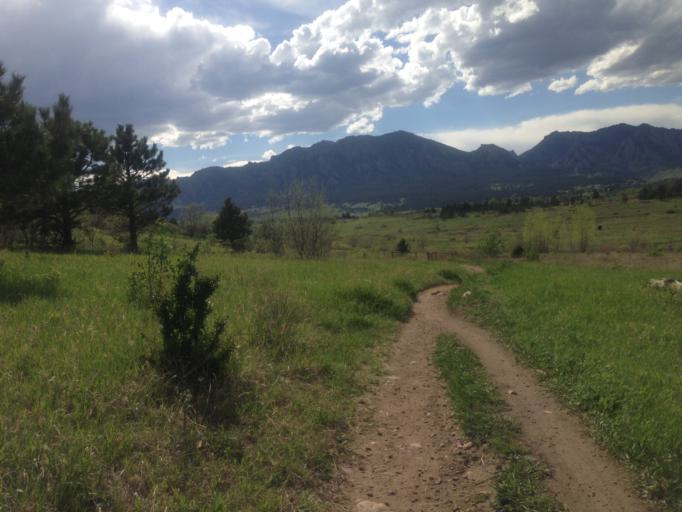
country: US
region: Colorado
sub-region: Boulder County
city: Superior
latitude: 39.9527
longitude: -105.2228
